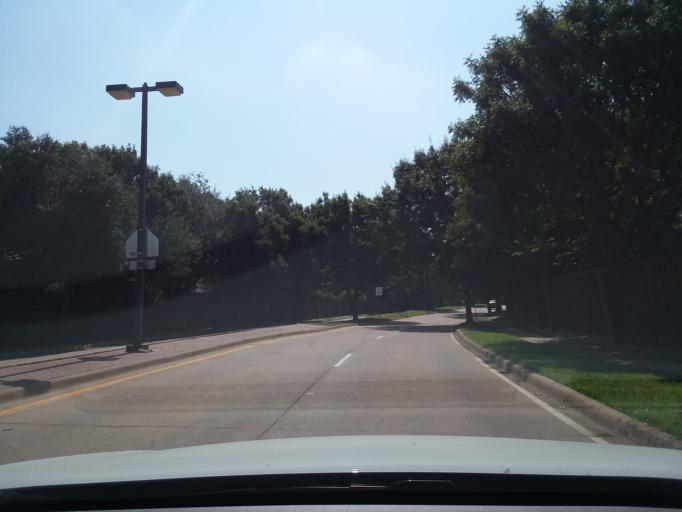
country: US
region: Texas
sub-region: Denton County
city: Flower Mound
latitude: 33.0199
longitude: -97.0593
